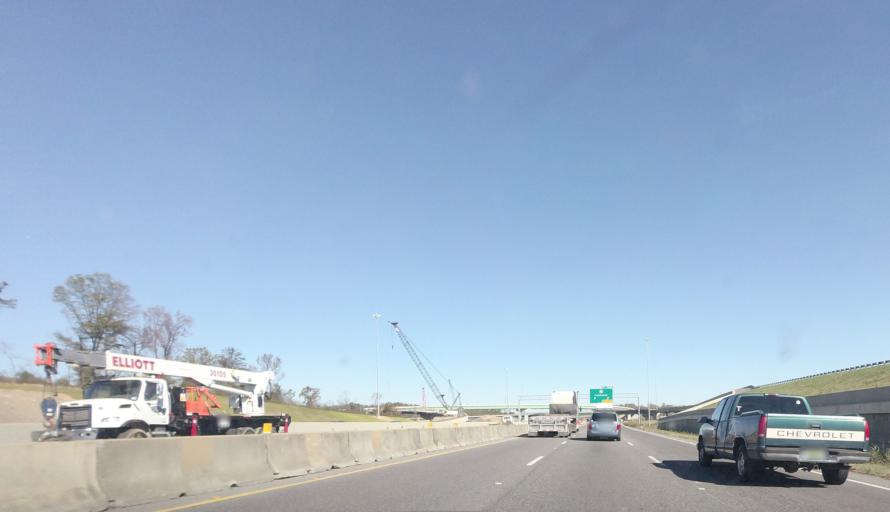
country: US
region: Alabama
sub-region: Jefferson County
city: Fultondale
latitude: 33.5689
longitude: -86.8202
